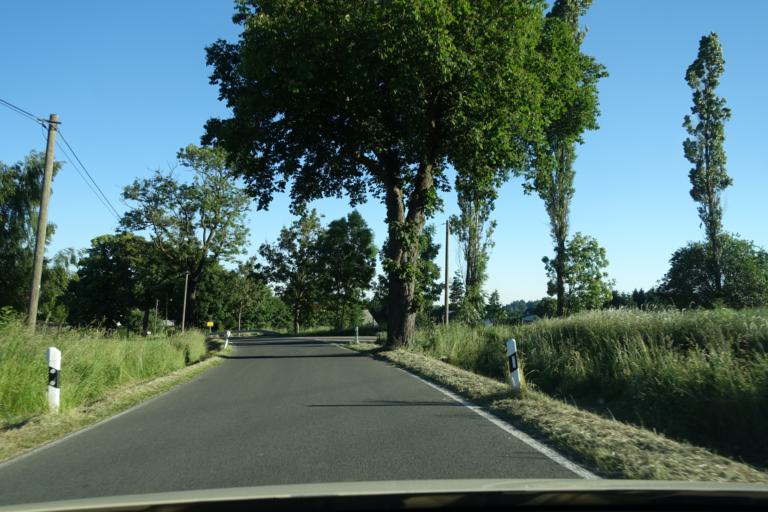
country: DE
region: Saxony
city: Grosshartmannsdorf
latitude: 50.8253
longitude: 13.2993
